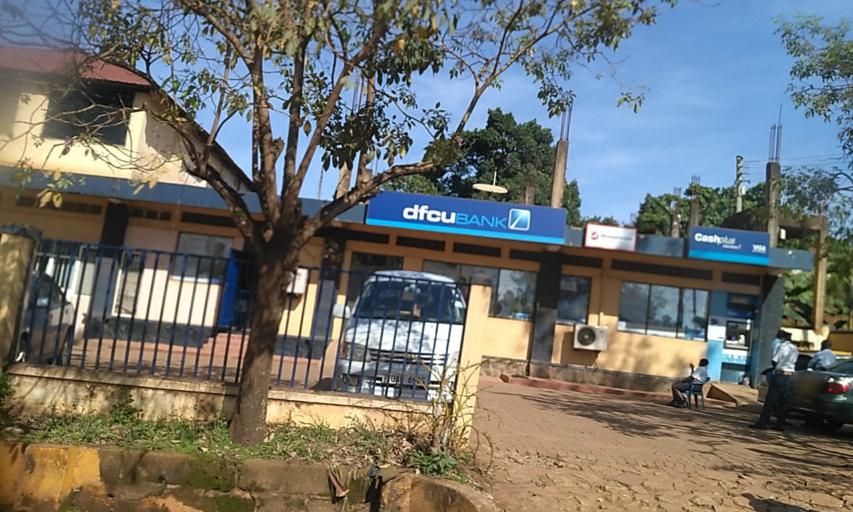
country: UG
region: Central Region
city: Kampala Central Division
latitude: 0.3421
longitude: 32.5631
